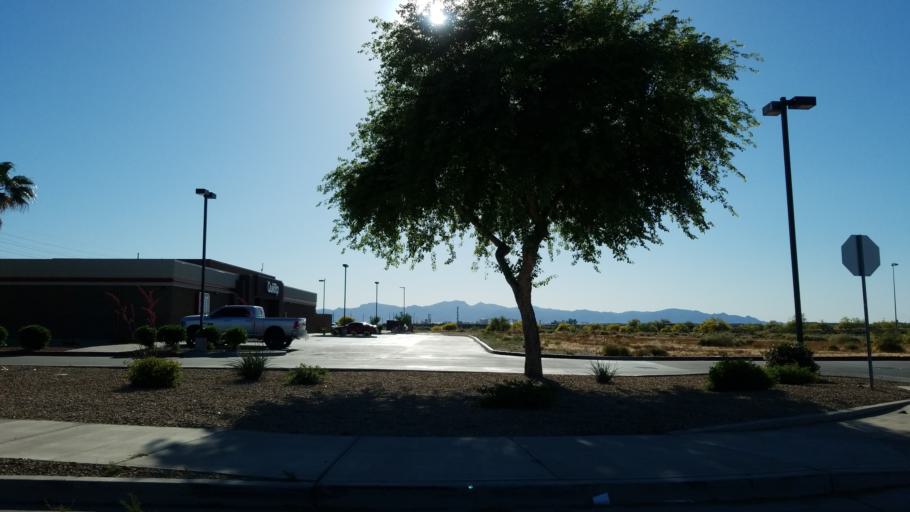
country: US
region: Arizona
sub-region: Maricopa County
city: Youngtown
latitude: 33.5663
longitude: -112.3092
